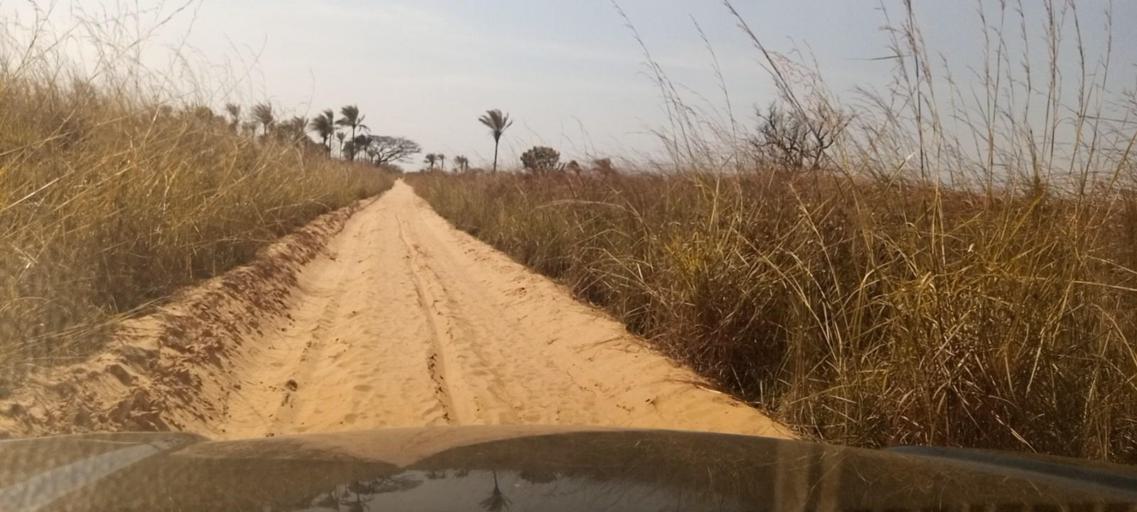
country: CD
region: Kasai-Oriental
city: Kabinda
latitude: -5.8006
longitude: 25.0293
